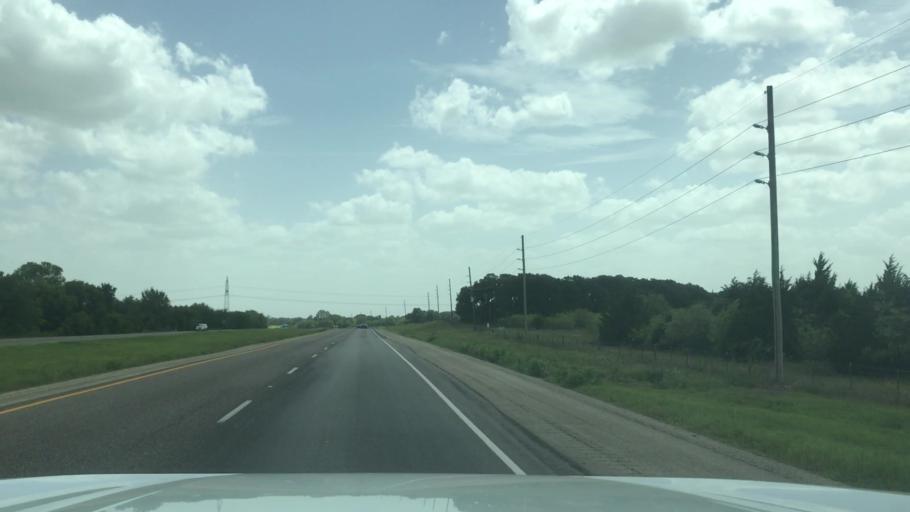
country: US
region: Texas
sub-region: Robertson County
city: Calvert
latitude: 31.1040
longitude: -96.7144
